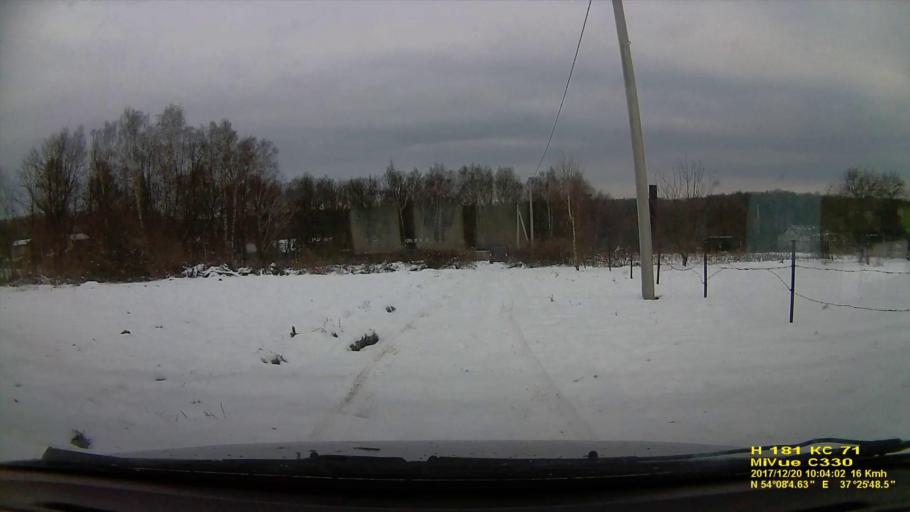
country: RU
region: Tula
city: Kosaya Gora
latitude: 54.1345
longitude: 37.4301
